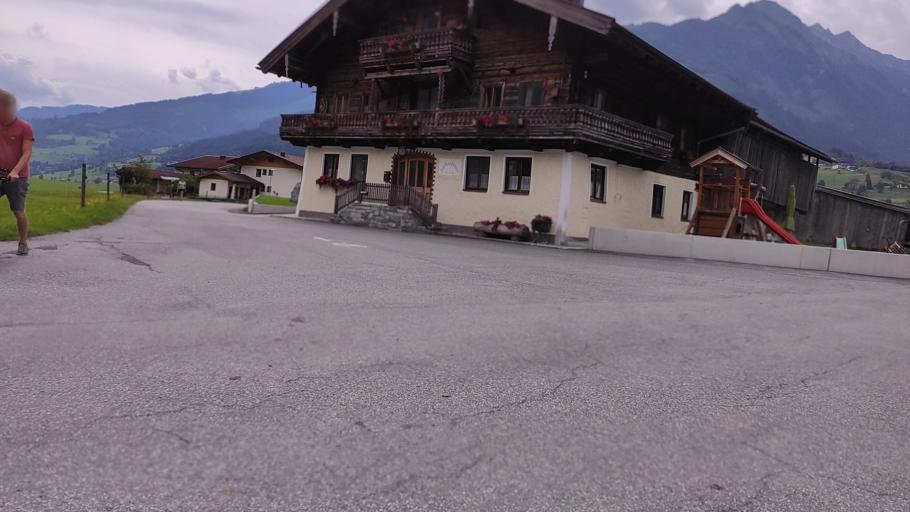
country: AT
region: Salzburg
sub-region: Politischer Bezirk Zell am See
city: Niedernsill
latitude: 47.2829
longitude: 12.6559
